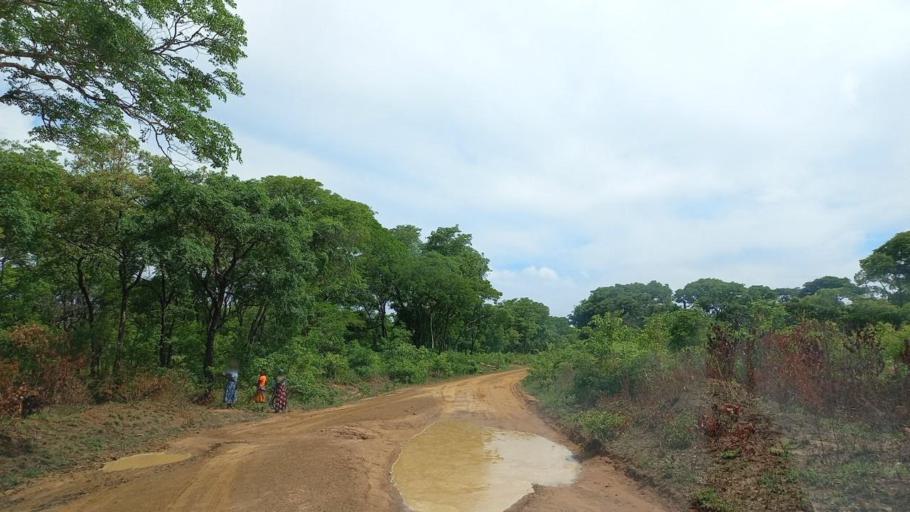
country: ZM
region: North-Western
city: Kabompo
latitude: -13.5399
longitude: 24.0994
